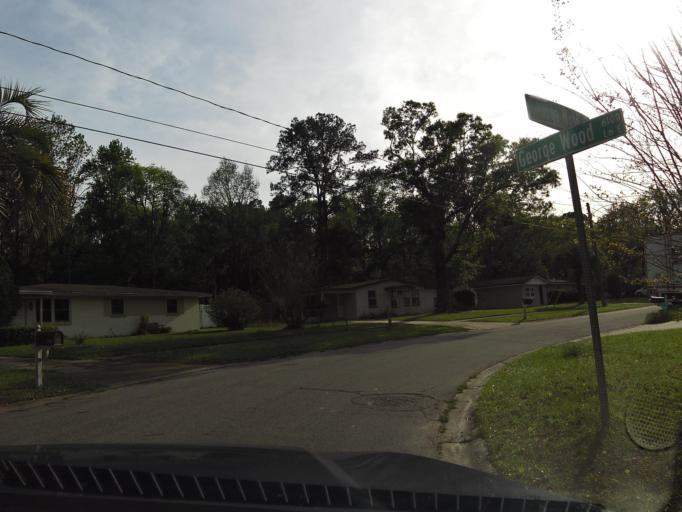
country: US
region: Florida
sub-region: Clay County
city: Bellair-Meadowbrook Terrace
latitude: 30.2377
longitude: -81.7588
